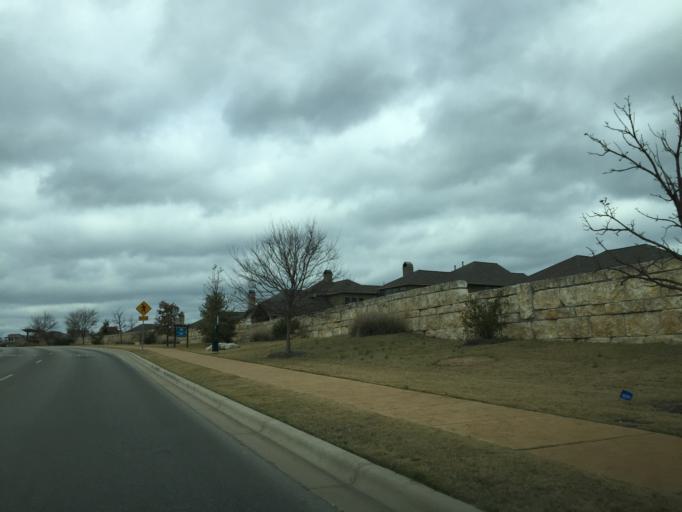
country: US
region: Texas
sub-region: Travis County
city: The Hills
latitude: 30.3507
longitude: -98.0090
